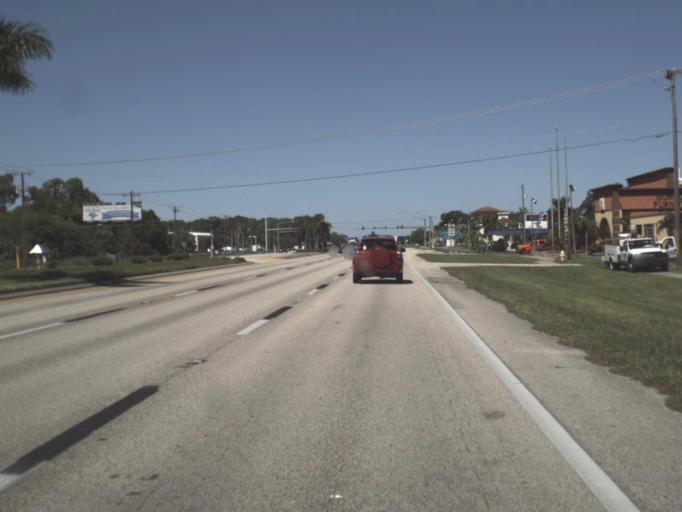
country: US
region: Florida
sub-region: Lee County
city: San Carlos Park
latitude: 26.4738
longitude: -81.8362
